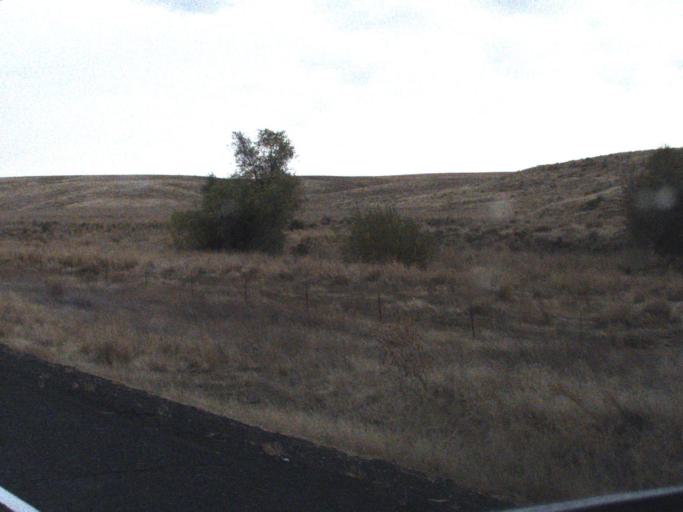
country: US
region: Washington
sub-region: Garfield County
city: Pomeroy
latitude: 46.7849
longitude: -117.9278
